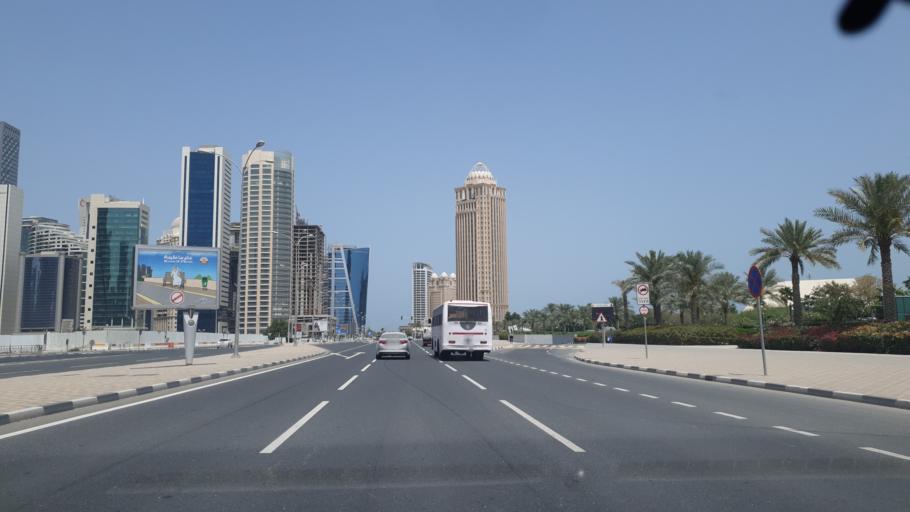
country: QA
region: Baladiyat ad Dawhah
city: Doha
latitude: 25.3198
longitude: 51.5329
